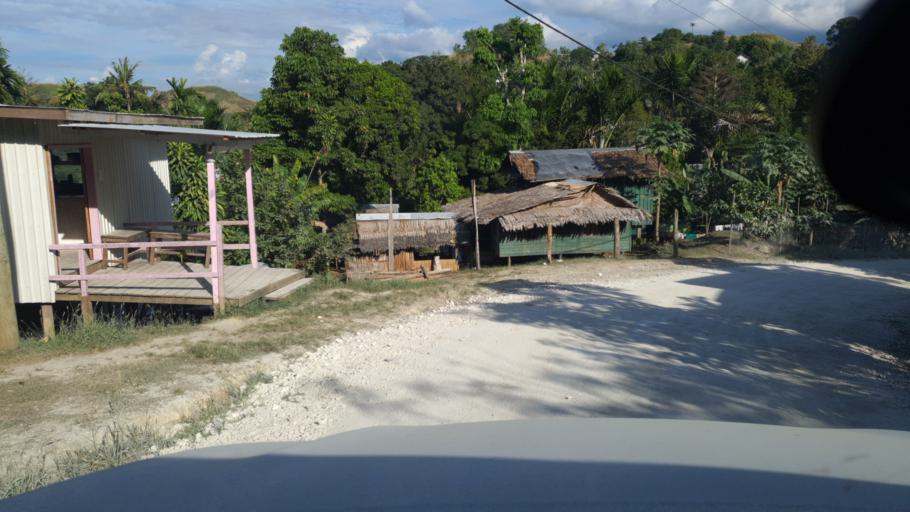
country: SB
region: Guadalcanal
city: Honiara
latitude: -9.4479
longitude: 159.9955
